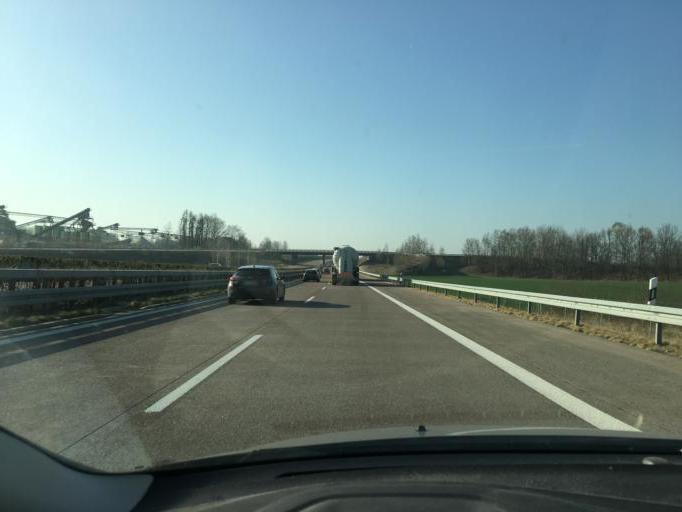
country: DE
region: Saxony
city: Penig
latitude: 50.9603
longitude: 12.6897
